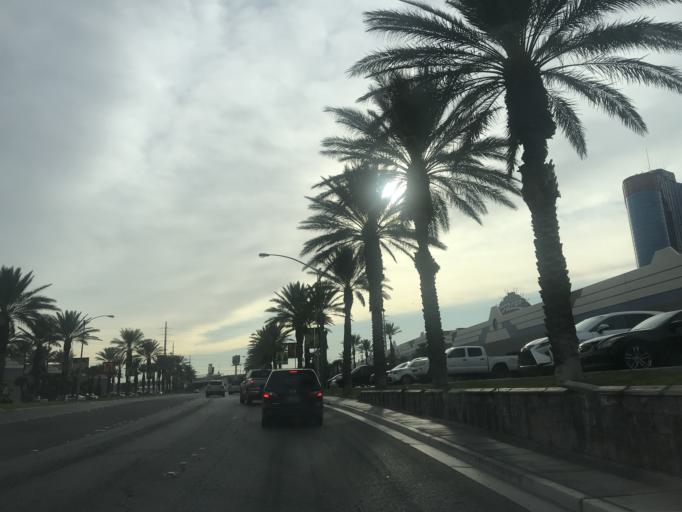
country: US
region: Nevada
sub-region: Clark County
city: Paradise
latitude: 36.1179
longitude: -115.1822
